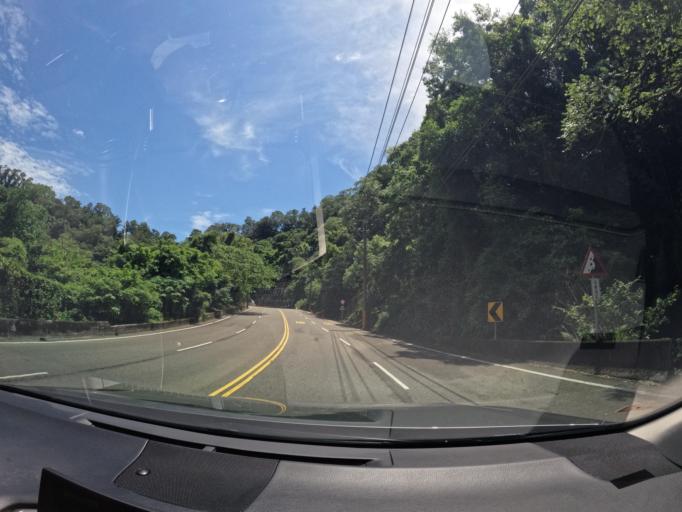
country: TW
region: Taiwan
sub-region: Miaoli
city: Miaoli
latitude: 24.5757
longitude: 120.9386
